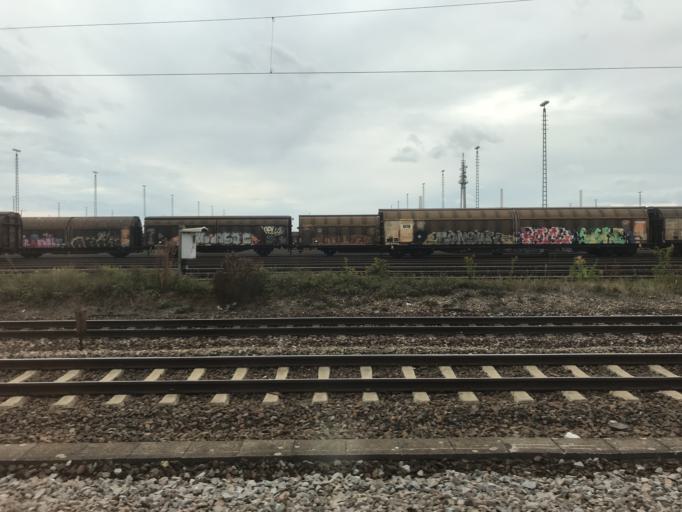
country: DE
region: Rheinland-Pfalz
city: Altrip
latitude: 49.4570
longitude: 8.5241
